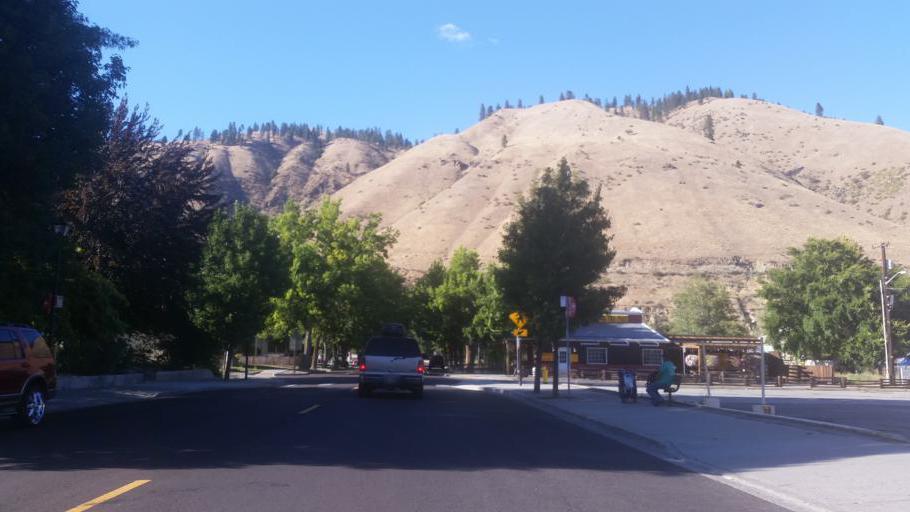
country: US
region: Washington
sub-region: Chelan County
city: Cashmere
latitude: 47.5232
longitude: -120.4700
